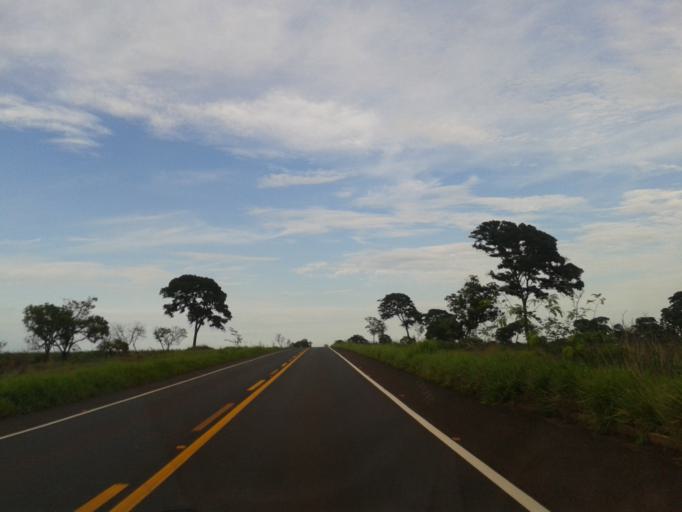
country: BR
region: Minas Gerais
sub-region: Santa Vitoria
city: Santa Vitoria
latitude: -19.0437
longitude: -50.4429
